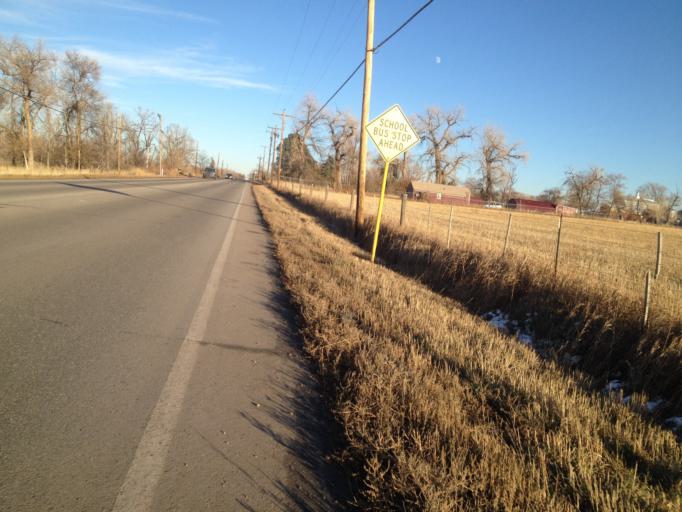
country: US
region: Colorado
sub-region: Boulder County
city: Louisville
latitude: 40.0146
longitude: -105.1565
